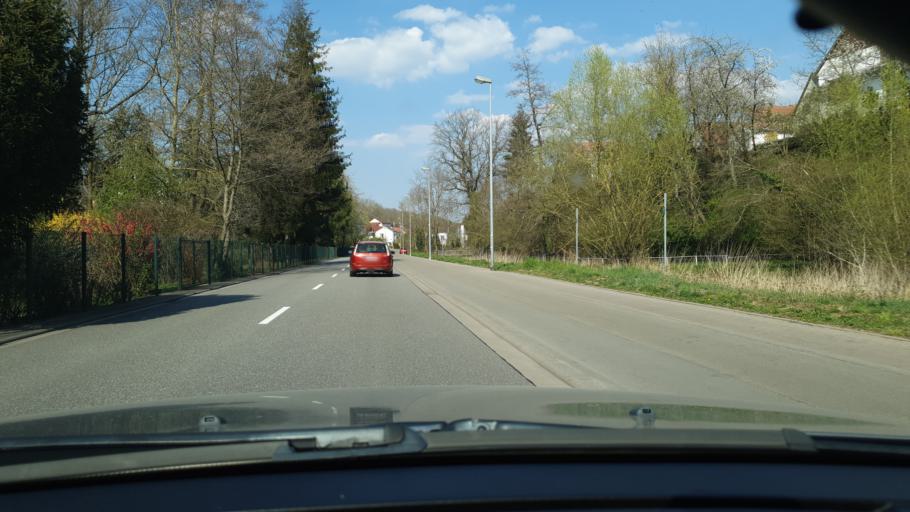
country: DE
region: Rheinland-Pfalz
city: Zweibrucken
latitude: 49.2557
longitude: 7.3950
